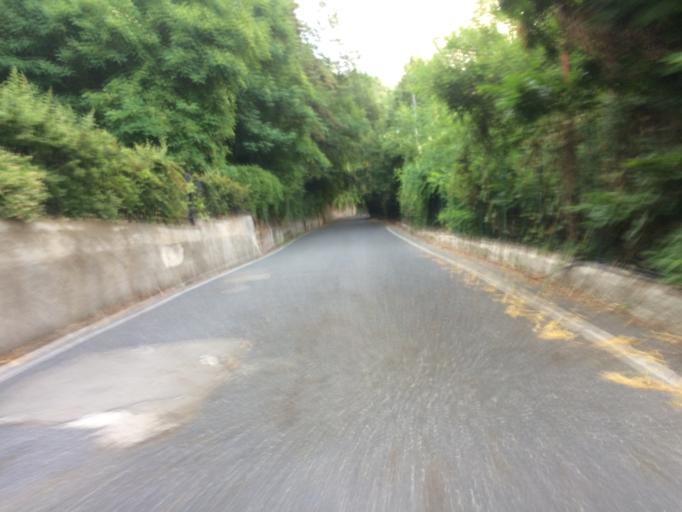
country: IT
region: Liguria
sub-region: Provincia di Imperia
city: Seborga
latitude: 43.8522
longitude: 7.7207
